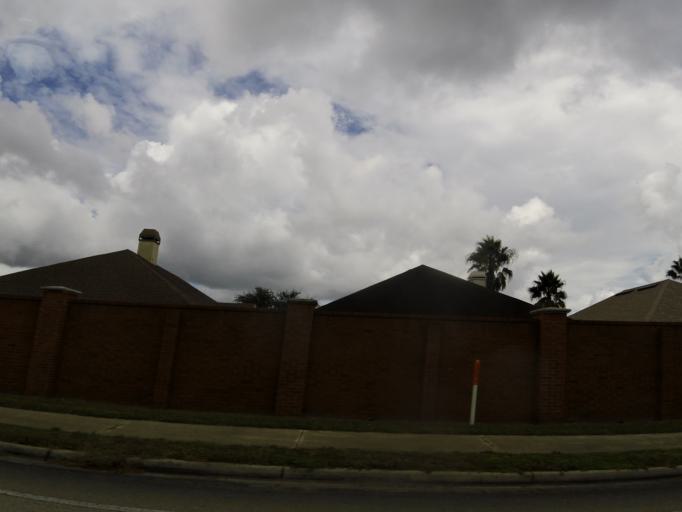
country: US
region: Florida
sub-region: Clay County
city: Lakeside
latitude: 30.1021
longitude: -81.7352
